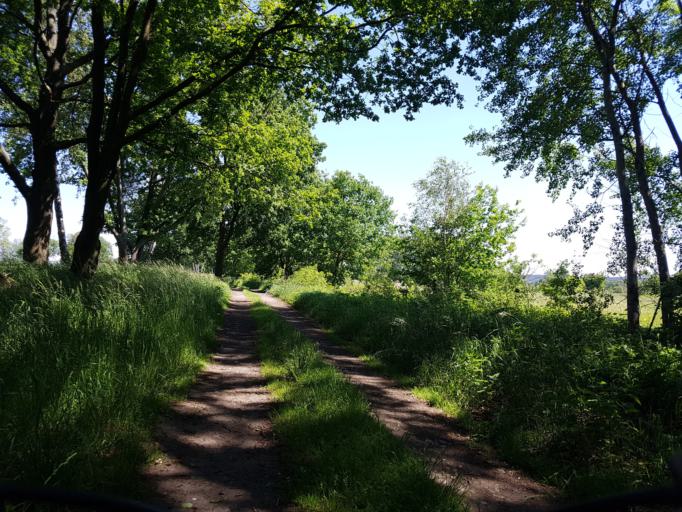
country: DE
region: Brandenburg
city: Merzdorf
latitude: 51.4322
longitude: 13.5416
